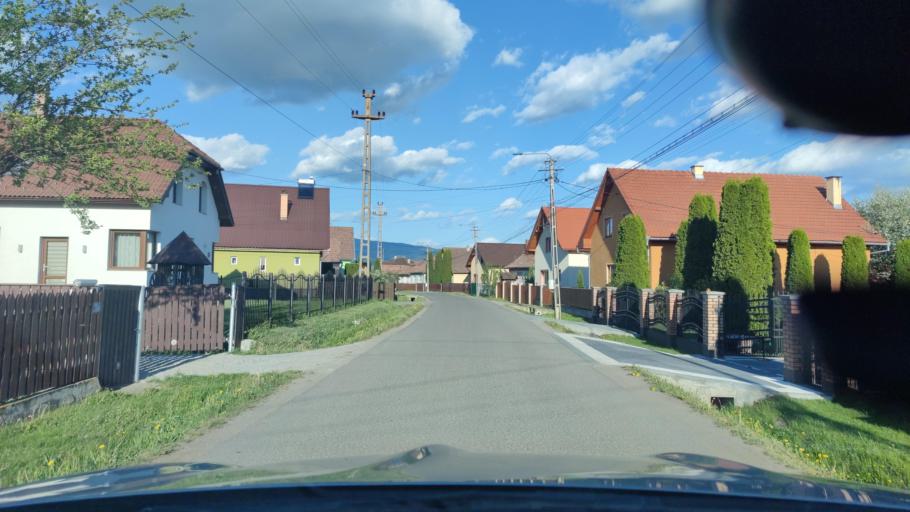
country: RO
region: Harghita
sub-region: Comuna Remetea
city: Remetea
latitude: 46.7946
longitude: 25.4495
